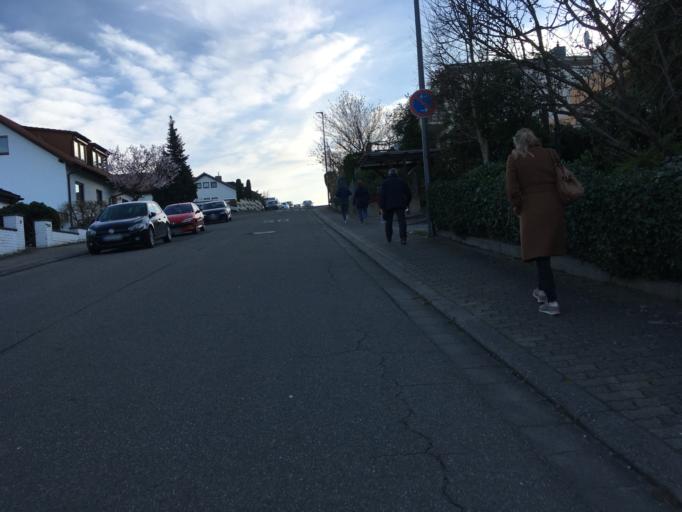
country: DE
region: Rheinland-Pfalz
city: Deidesheim
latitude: 49.3834
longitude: 8.1577
